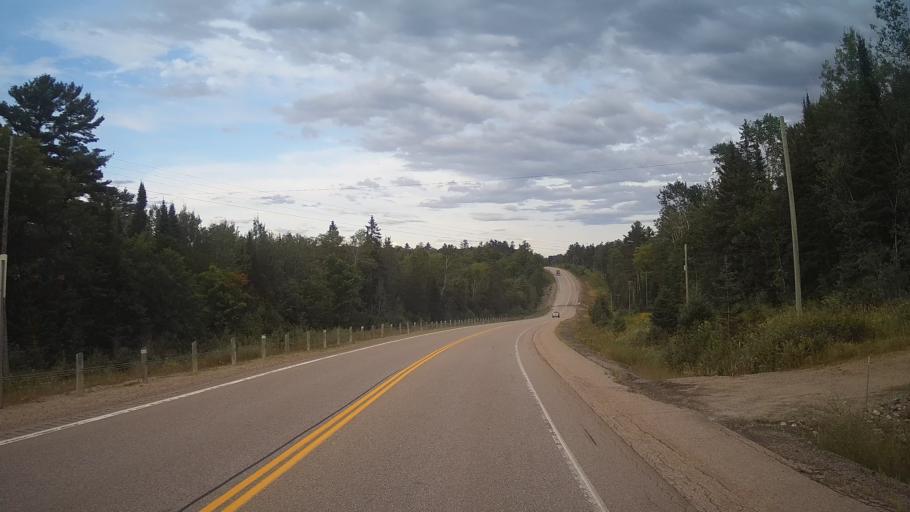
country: CA
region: Ontario
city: Mattawa
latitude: 46.2429
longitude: -78.1293
